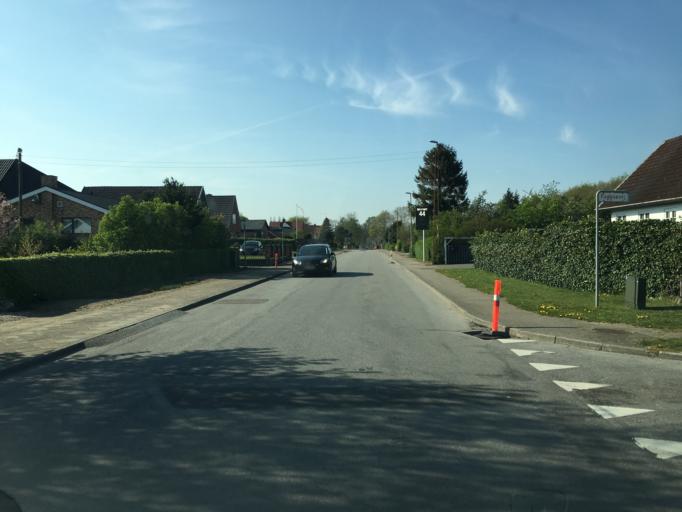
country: DK
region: South Denmark
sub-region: Haderslev Kommune
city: Vojens
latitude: 55.2461
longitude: 9.3154
